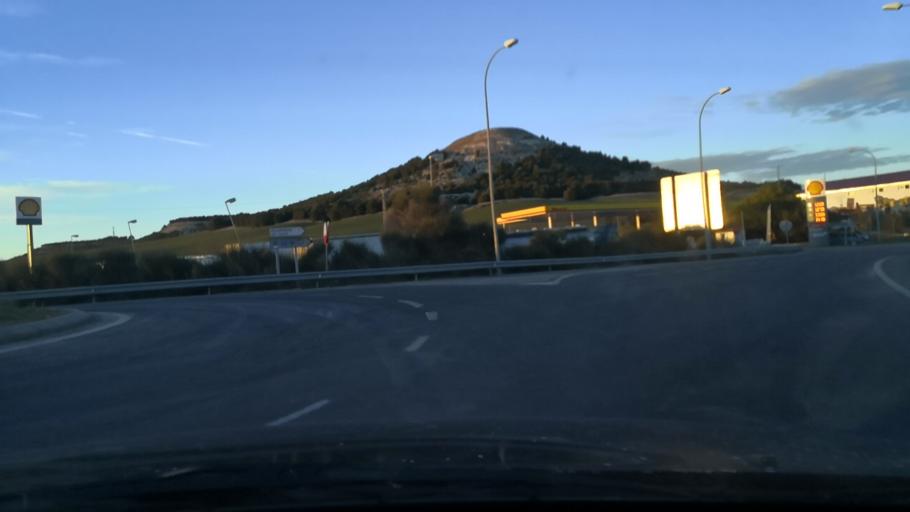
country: ES
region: Castille and Leon
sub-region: Provincia de Valladolid
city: Bercero
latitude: 41.5251
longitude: -5.0424
